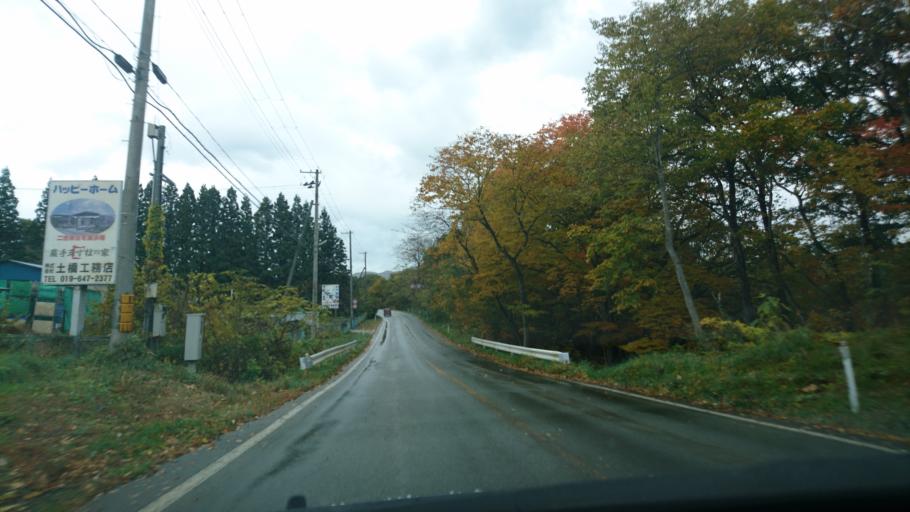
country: JP
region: Iwate
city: Shizukuishi
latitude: 39.6684
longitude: 140.9764
